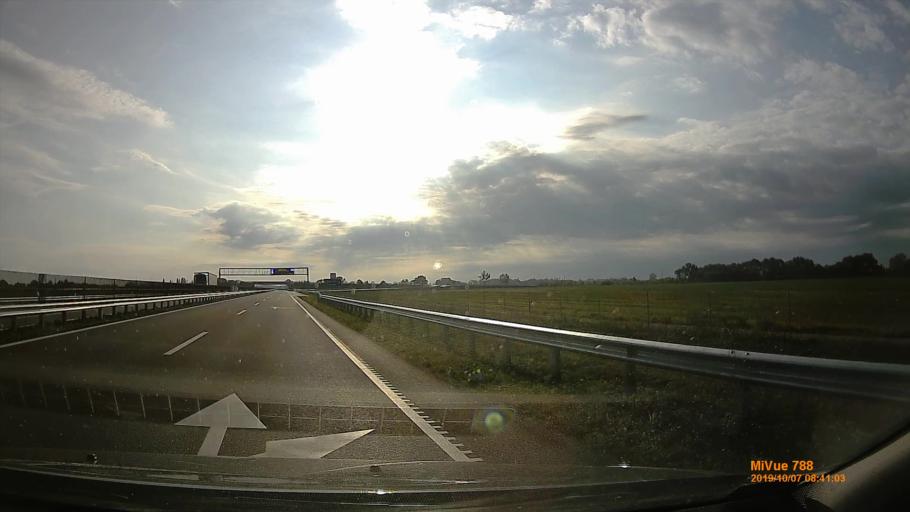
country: HU
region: Bekes
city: Bekesszentandras
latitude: 46.8202
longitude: 20.5098
